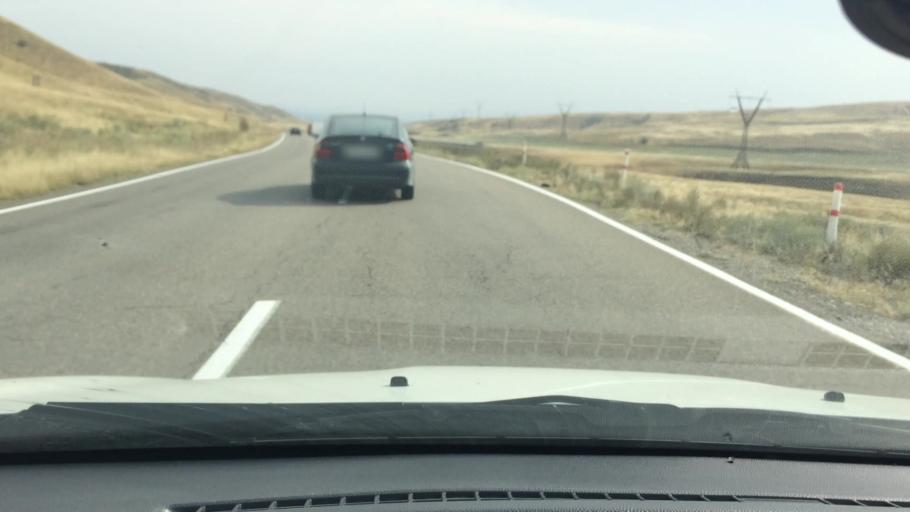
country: GE
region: Kvemo Kartli
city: Rust'avi
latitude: 41.5023
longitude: 44.9551
